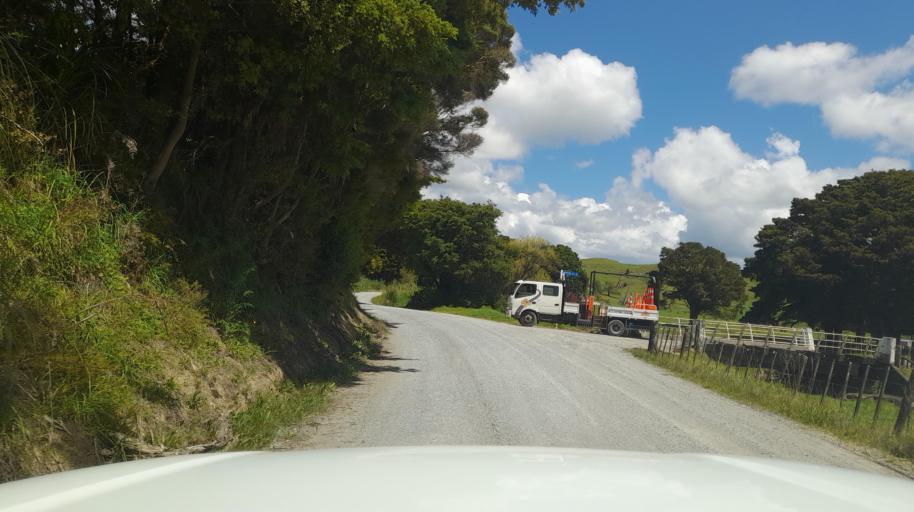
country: NZ
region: Northland
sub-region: Far North District
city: Kaitaia
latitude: -35.1152
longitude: 173.3946
